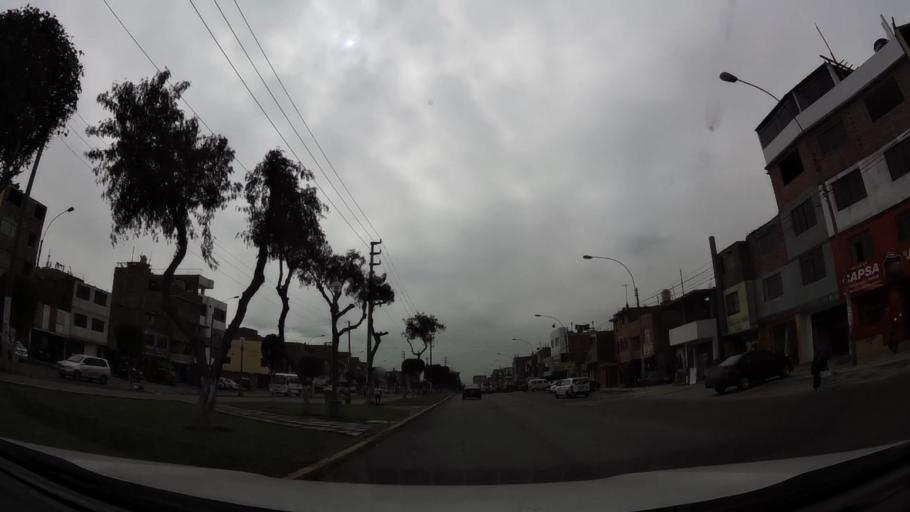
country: PE
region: Callao
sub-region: Callao
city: Callao
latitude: -12.0236
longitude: -77.0992
